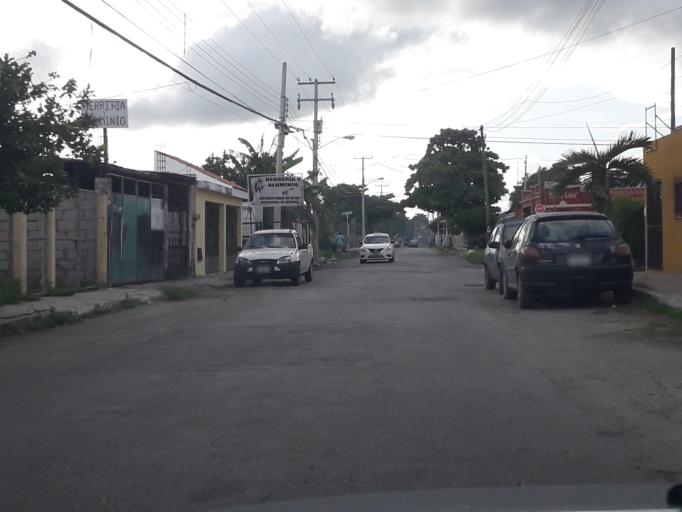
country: MX
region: Yucatan
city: Merida
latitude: 20.9611
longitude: -89.6578
